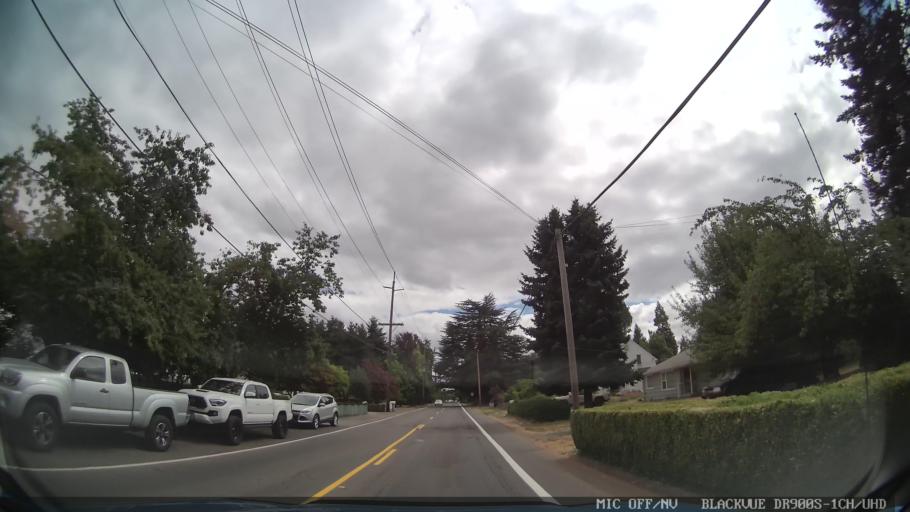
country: US
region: Oregon
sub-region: Marion County
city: Four Corners
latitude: 44.9534
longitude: -123.0009
